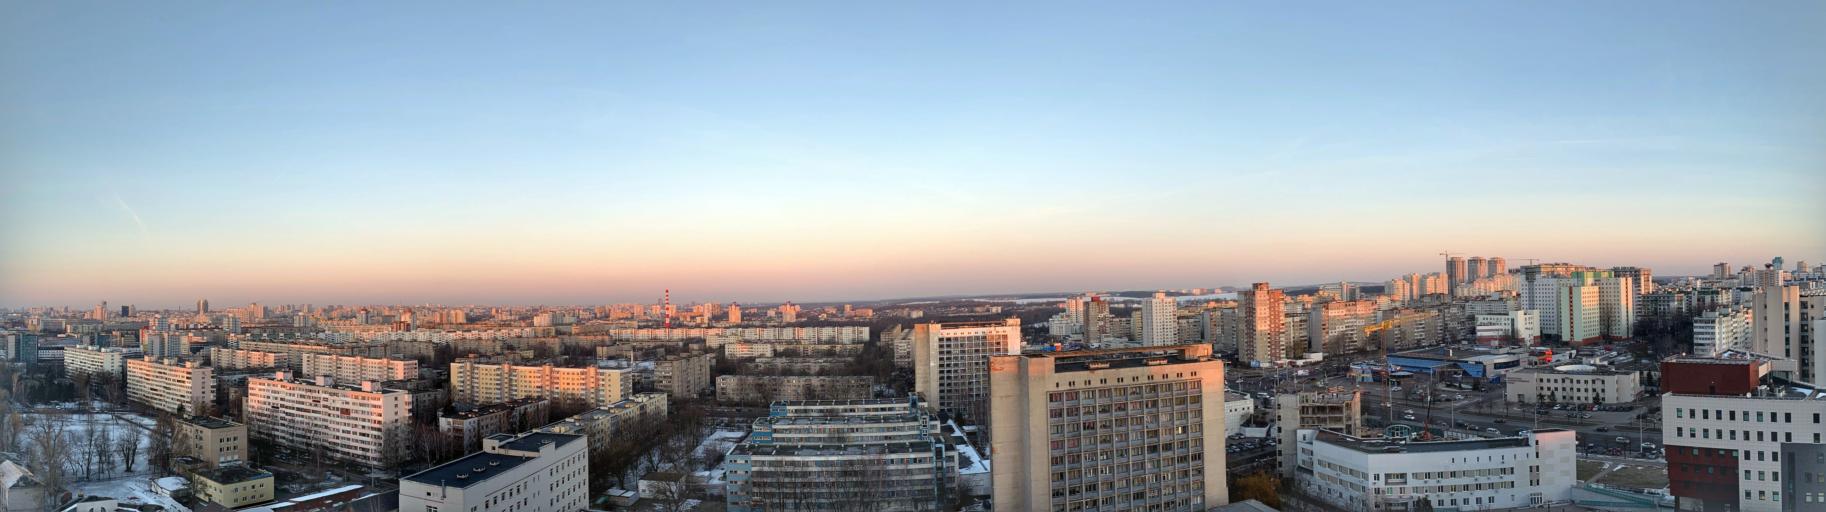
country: BY
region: Minsk
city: Minsk
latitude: 53.9257
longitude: 27.5893
